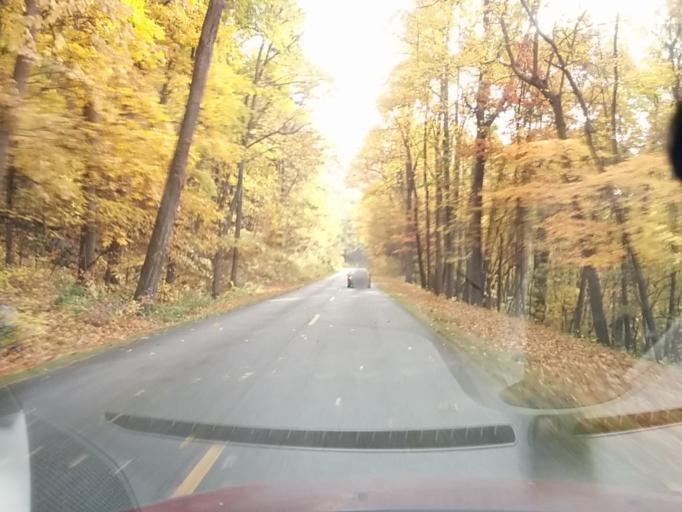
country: US
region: Virginia
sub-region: City of Buena Vista
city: Buena Vista
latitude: 37.7967
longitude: -79.2004
